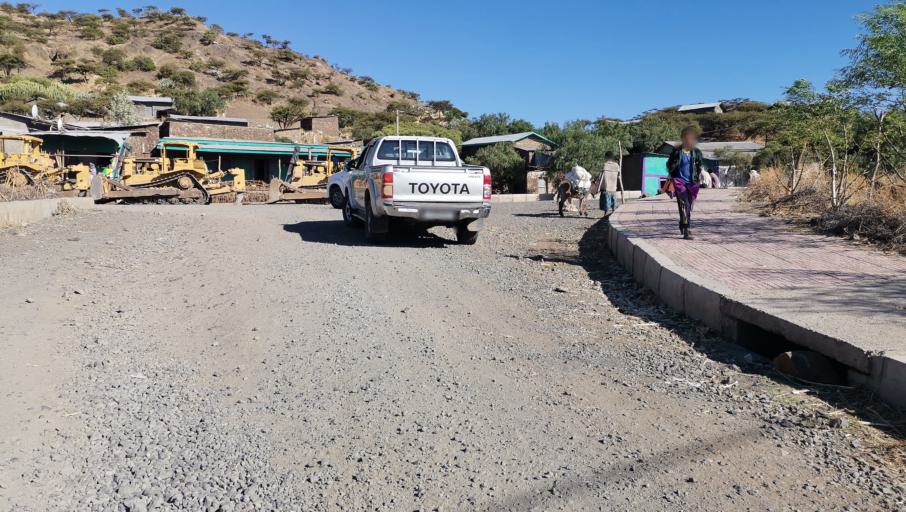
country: ET
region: Tigray
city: Korem
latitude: 12.5195
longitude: 39.0780
